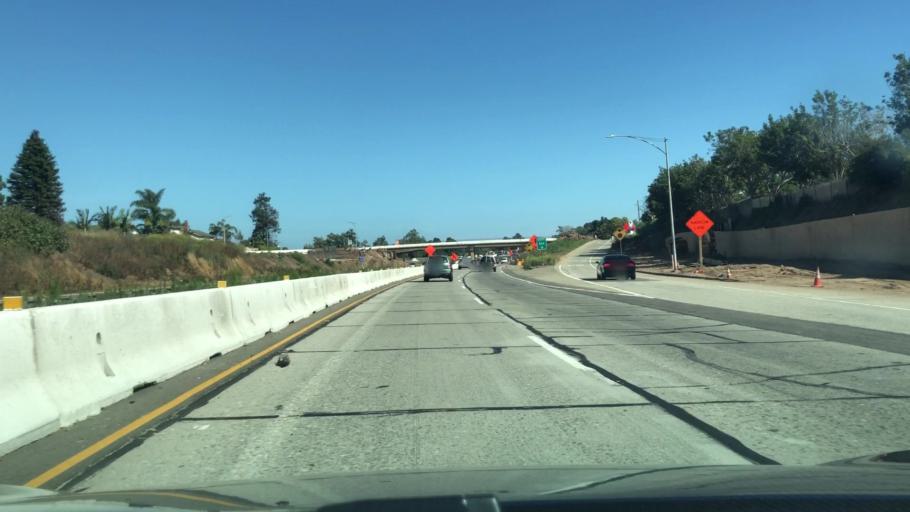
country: US
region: California
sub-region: Santa Barbara County
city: Carpinteria
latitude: 34.3987
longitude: -119.5131
